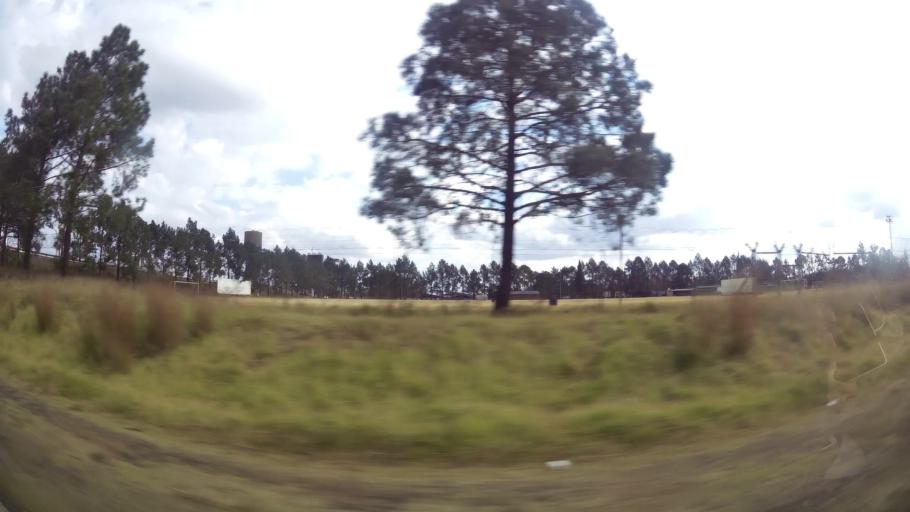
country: ZA
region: Orange Free State
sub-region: Fezile Dabi District Municipality
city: Sasolburg
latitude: -26.8168
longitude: 27.8422
